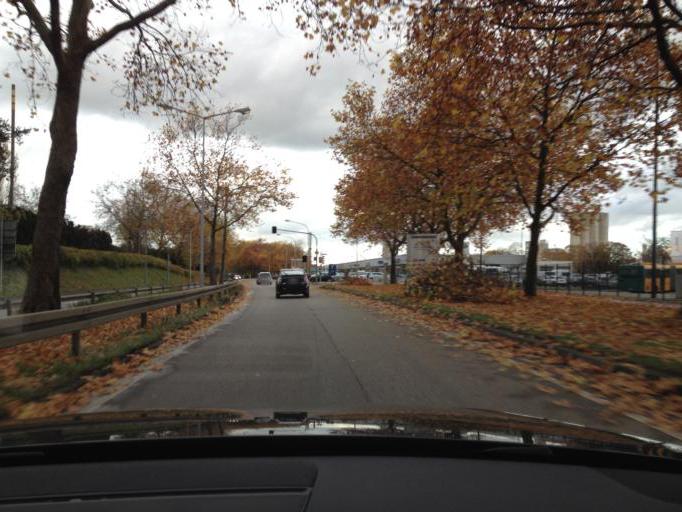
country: DE
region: Baden-Wuerttemberg
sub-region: Regierungsbezirk Stuttgart
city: Heilbronn
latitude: 49.1450
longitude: 9.2000
